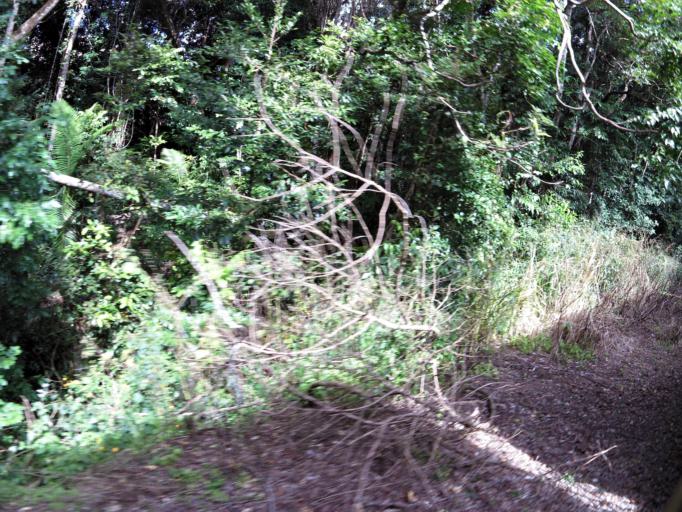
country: AU
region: Queensland
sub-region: Tablelands
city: Kuranda
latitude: -16.8253
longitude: 145.6397
